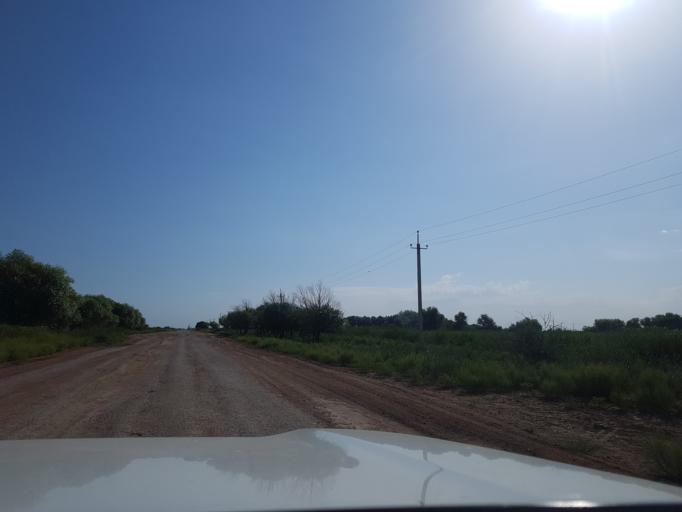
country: TM
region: Dasoguz
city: Koeneuergench
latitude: 42.0443
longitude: 58.8215
